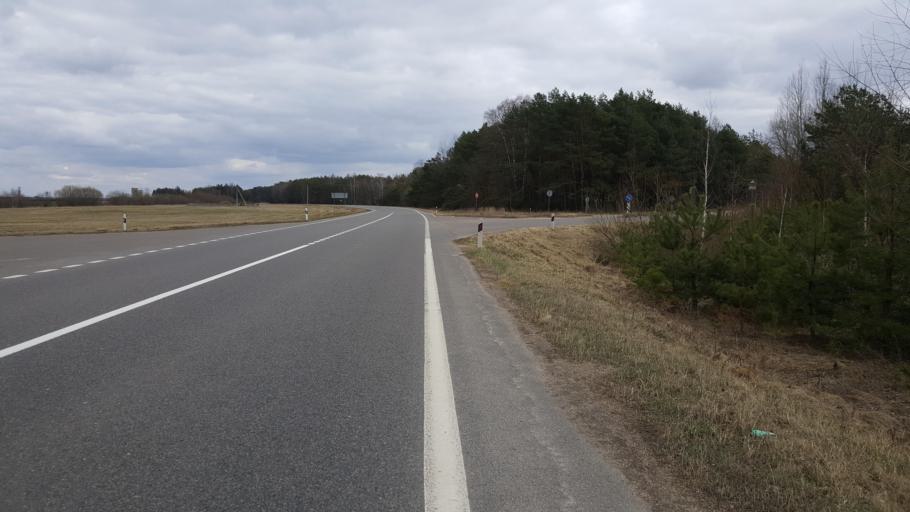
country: BY
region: Brest
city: Kamyanyuki
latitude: 52.5053
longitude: 23.7067
